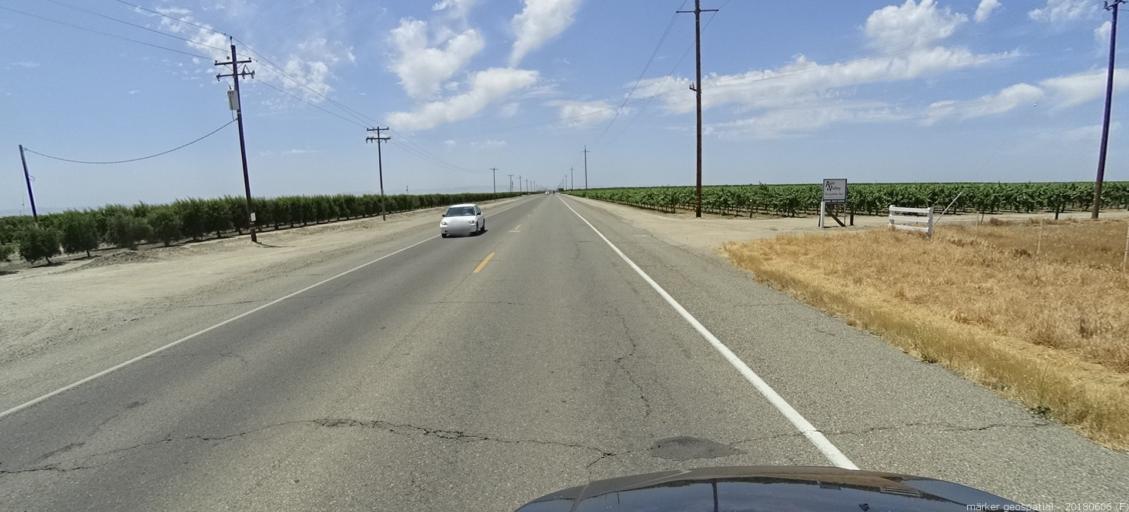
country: US
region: California
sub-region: Fresno County
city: Firebaugh
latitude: 36.8588
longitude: -120.3541
